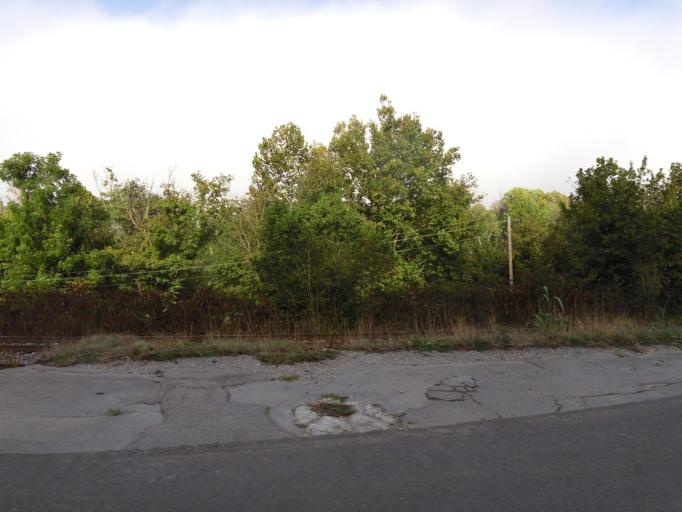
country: US
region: Tennessee
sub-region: Campbell County
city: Jellico
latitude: 36.5940
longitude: -84.1265
